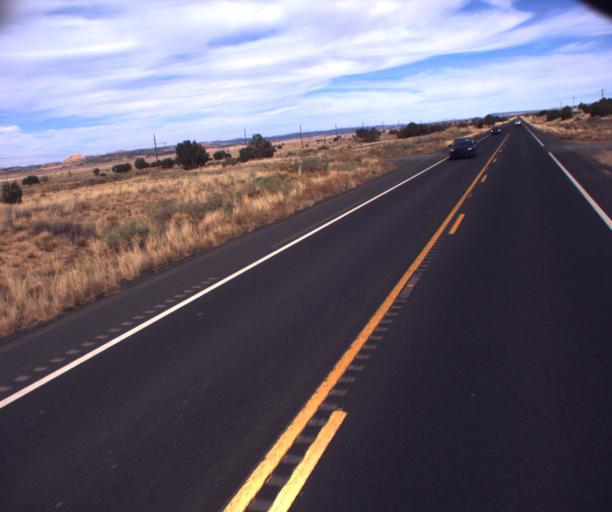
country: US
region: Arizona
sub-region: Coconino County
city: Kaibito
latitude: 36.4781
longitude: -110.6527
